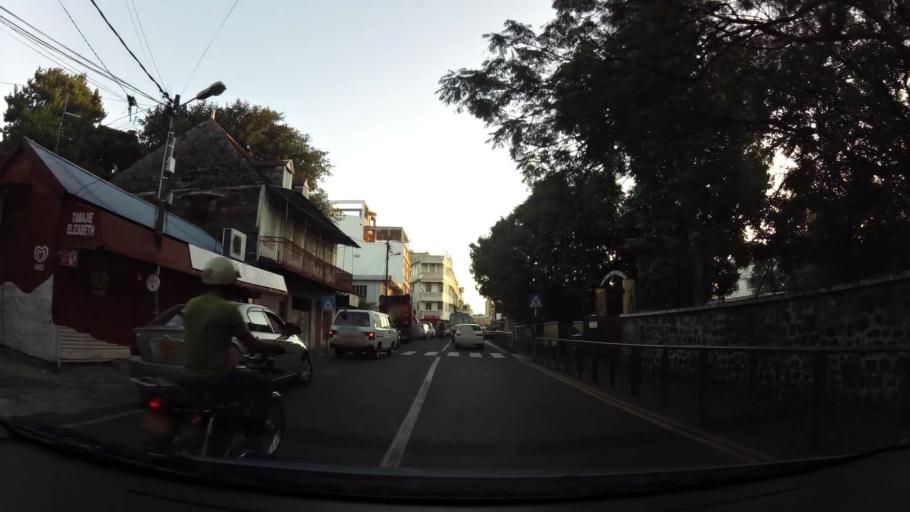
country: MU
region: Port Louis
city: Port Louis
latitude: -20.1579
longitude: 57.5140
